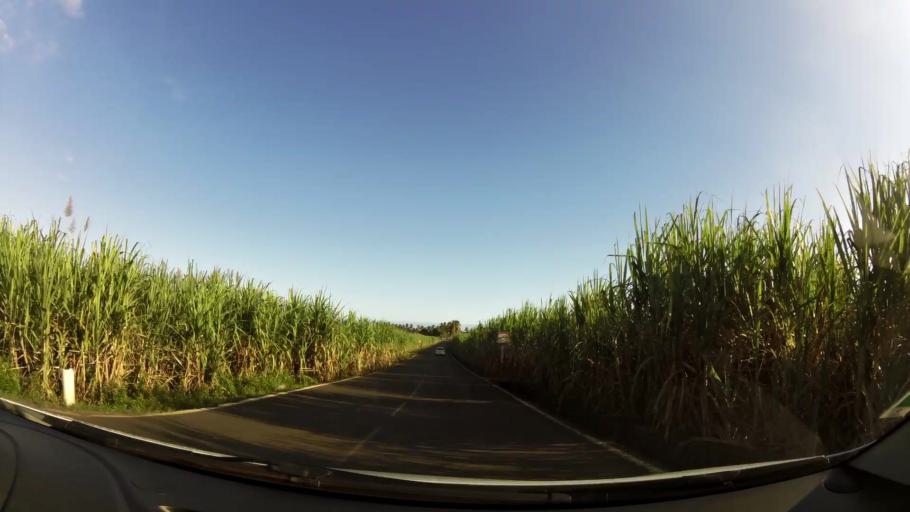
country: RE
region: Reunion
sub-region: Reunion
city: Saint-Louis
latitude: -21.2657
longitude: 55.3800
